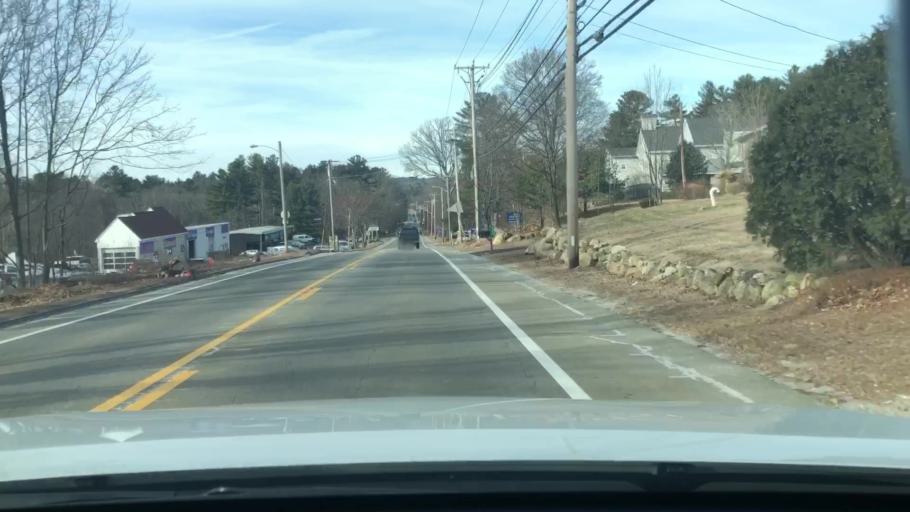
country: US
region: Massachusetts
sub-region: Worcester County
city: Hopedale
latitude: 42.1454
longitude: -71.5499
